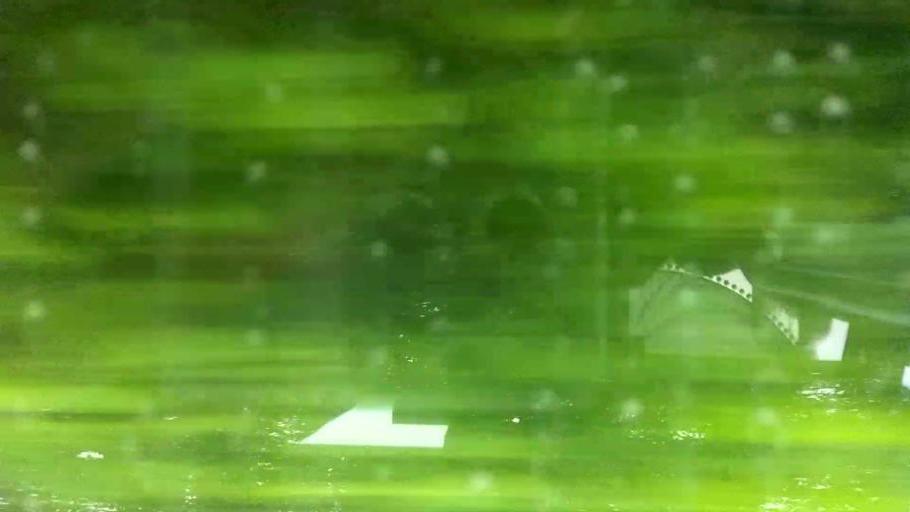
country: RU
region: Moskovskaya
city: Ozherel'ye
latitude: 54.8517
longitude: 38.2638
